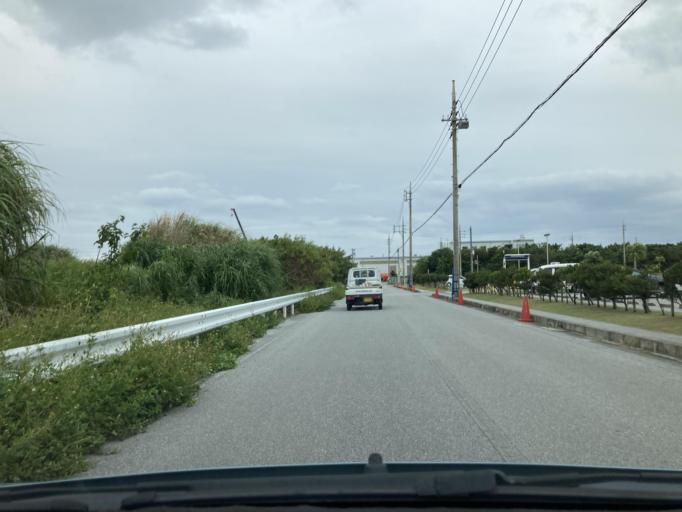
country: JP
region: Okinawa
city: Itoman
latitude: 26.1315
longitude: 127.6539
